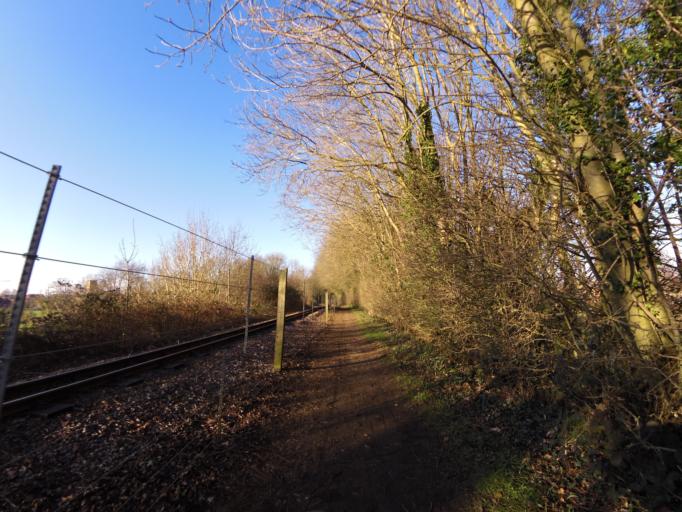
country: GB
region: England
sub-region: Norfolk
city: Coltishall
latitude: 52.7551
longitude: 1.3124
